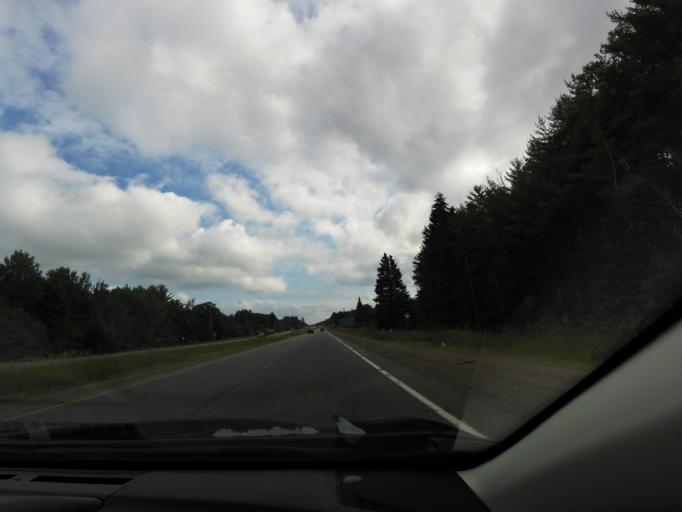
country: CA
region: Ontario
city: Bracebridge
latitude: 44.9995
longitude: -79.3037
